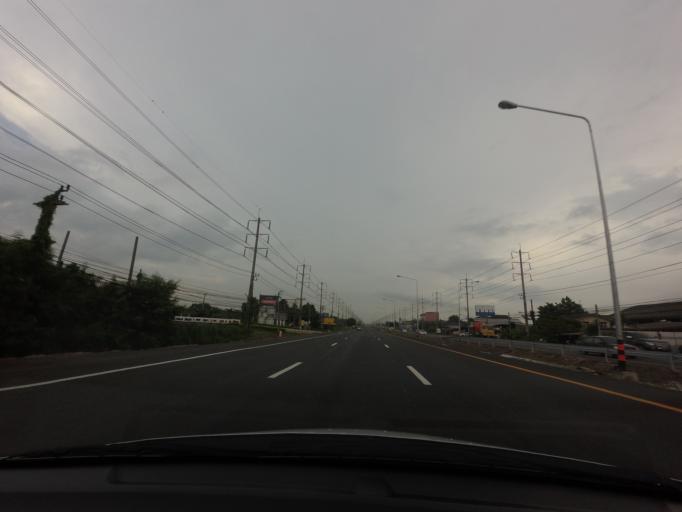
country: TH
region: Bangkok
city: Nong Chok
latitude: 13.8082
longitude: 100.8214
